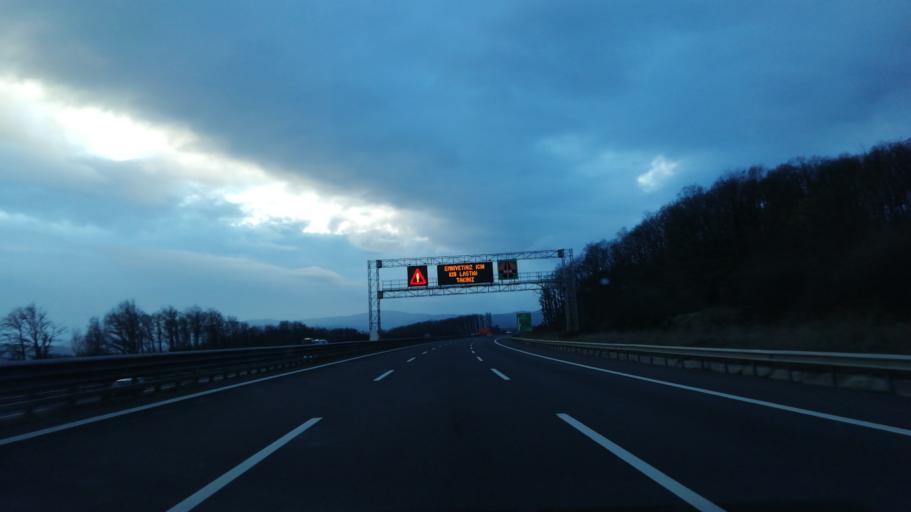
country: TR
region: Bolu
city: Bolu
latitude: 40.7214
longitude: 31.4926
